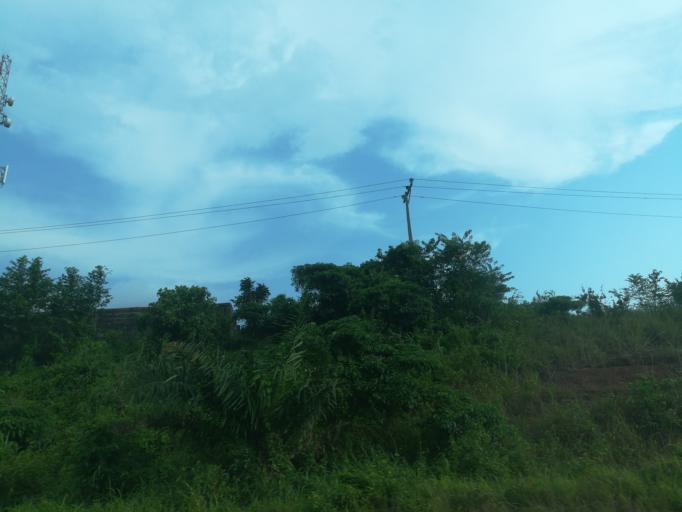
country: NG
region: Lagos
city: Ikorodu
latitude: 6.6223
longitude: 3.6603
